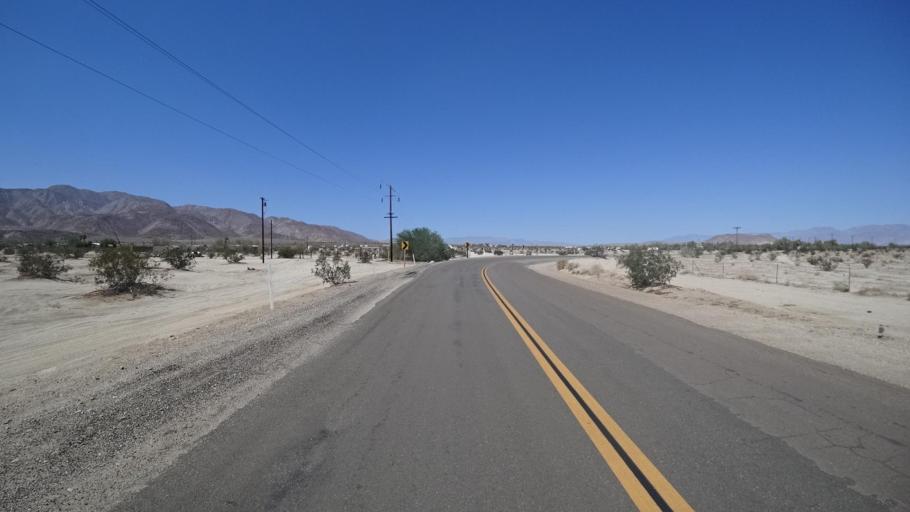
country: US
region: California
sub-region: Imperial County
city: Salton City
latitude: 33.1064
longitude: -116.1322
